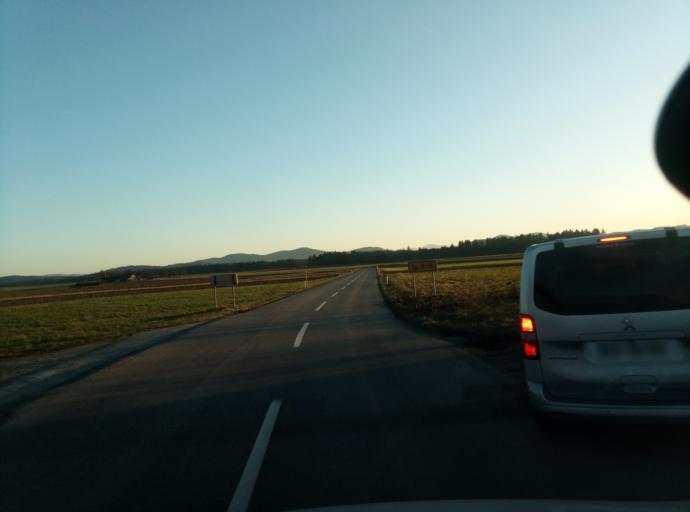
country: SI
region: Cerklje na Gorenjskem
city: Cerklje na Gorenjskem
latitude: 46.2259
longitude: 14.4867
